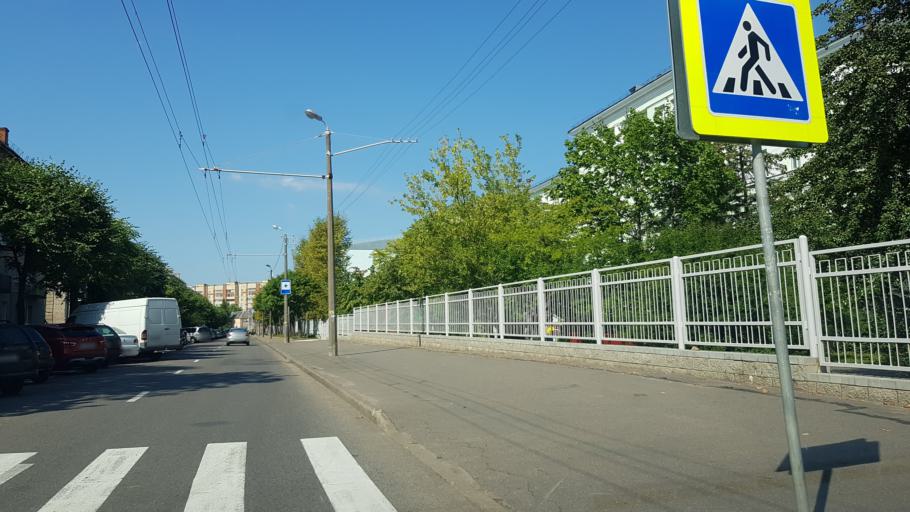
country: BY
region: Minsk
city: Minsk
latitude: 53.8916
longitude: 27.5195
